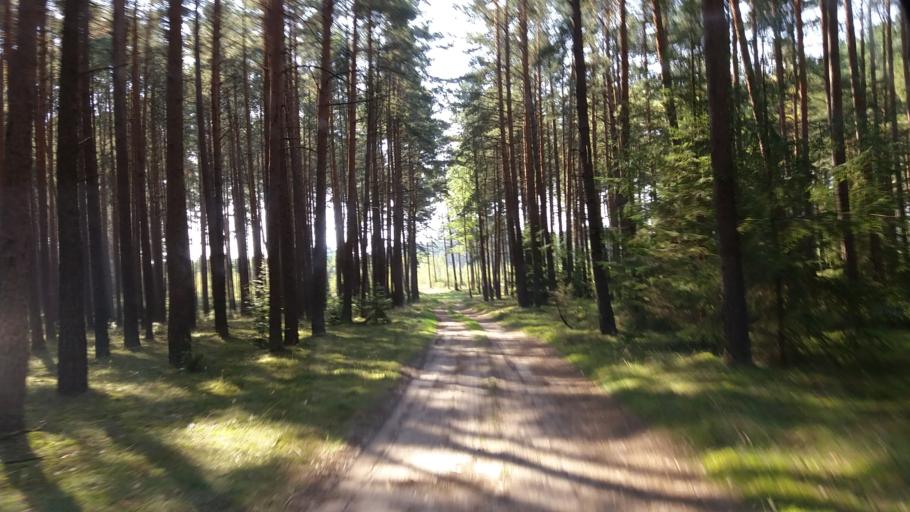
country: PL
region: West Pomeranian Voivodeship
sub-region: Powiat drawski
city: Kalisz Pomorski
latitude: 53.2122
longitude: 15.8975
